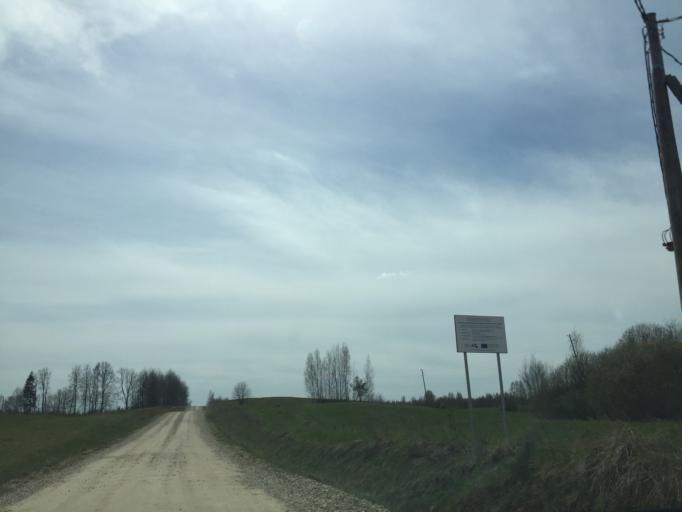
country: LV
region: Ludzas Rajons
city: Ludza
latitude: 56.5440
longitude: 27.5261
